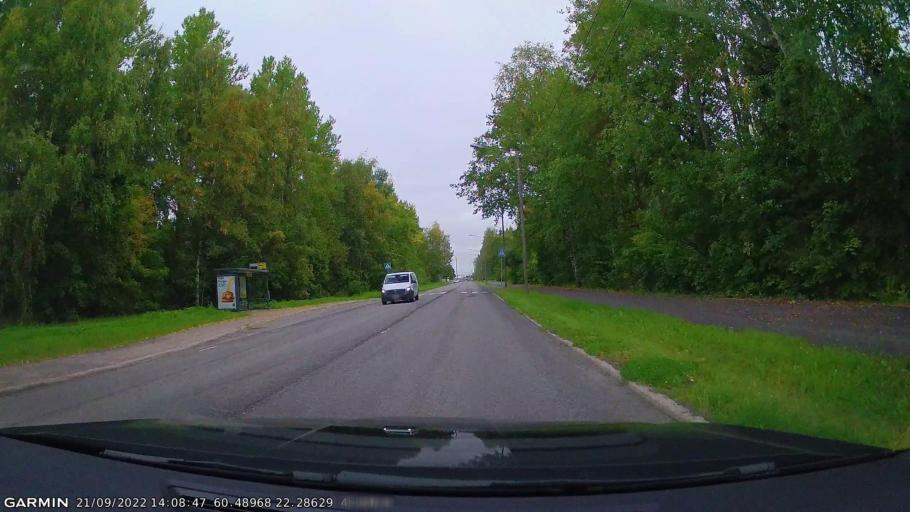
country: FI
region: Varsinais-Suomi
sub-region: Turku
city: Turku
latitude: 60.4898
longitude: 22.2864
